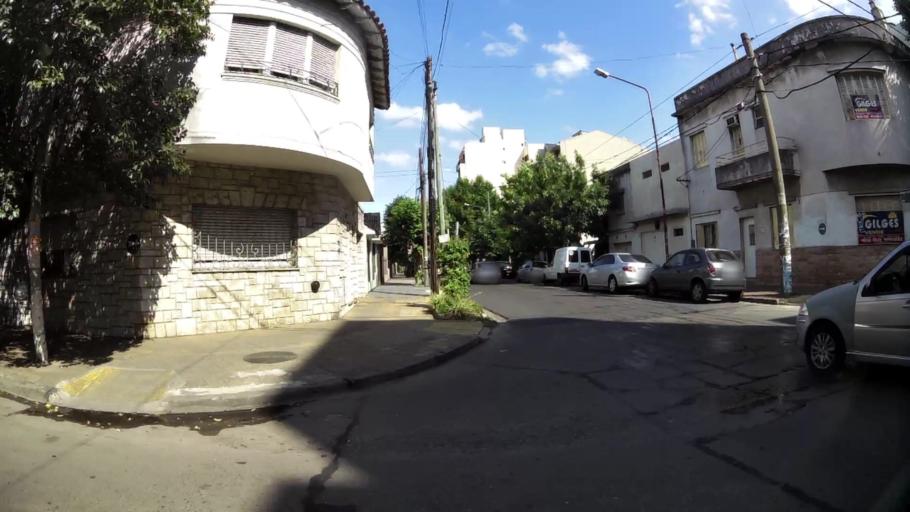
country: AR
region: Buenos Aires
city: San Justo
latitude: -34.6433
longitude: -58.5604
